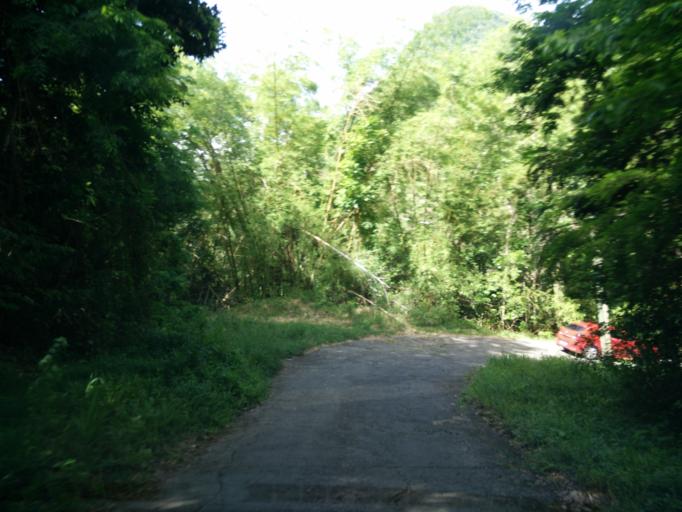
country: MQ
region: Martinique
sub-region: Martinique
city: Saint-Pierre
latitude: 14.7170
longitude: -61.1618
